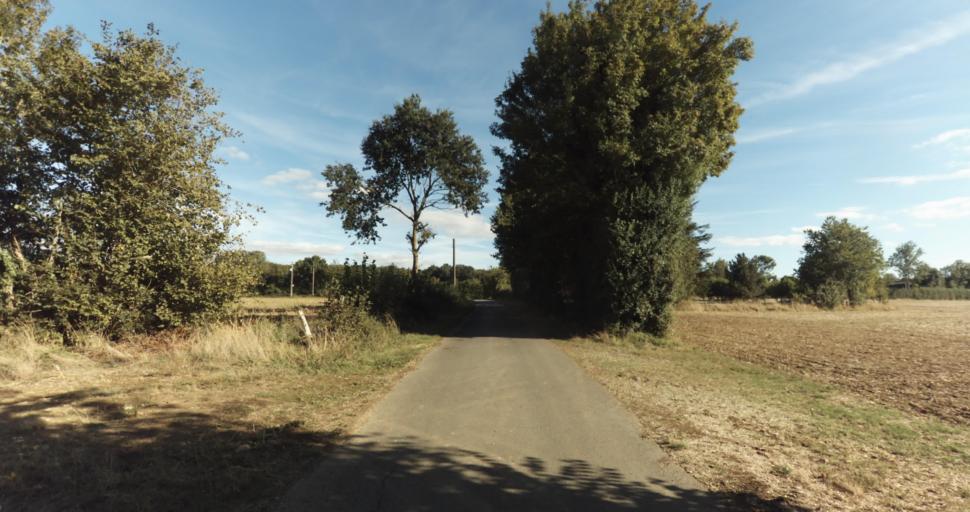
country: FR
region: Lower Normandy
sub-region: Departement de l'Orne
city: Vimoutiers
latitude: 48.9096
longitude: 0.1408
